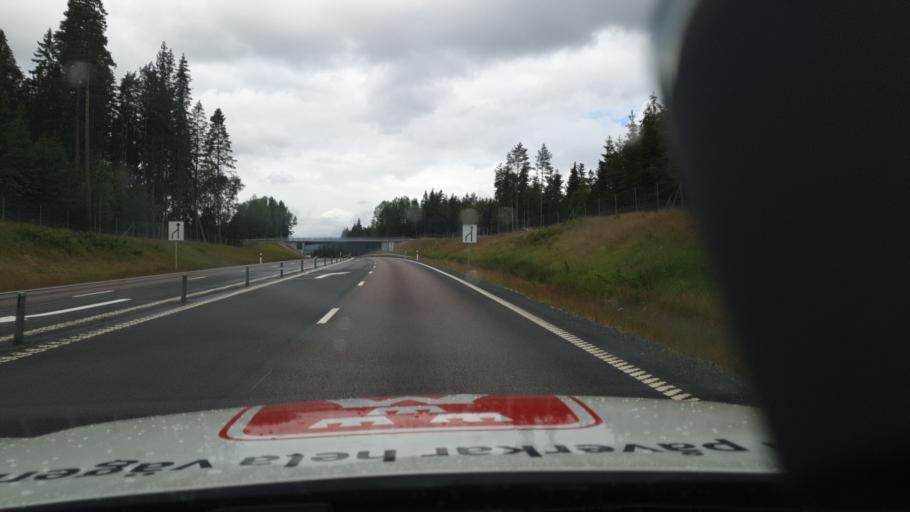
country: SE
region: Joenkoeping
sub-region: Mullsjo Kommun
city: Mullsjoe
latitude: 57.8927
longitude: 13.8853
